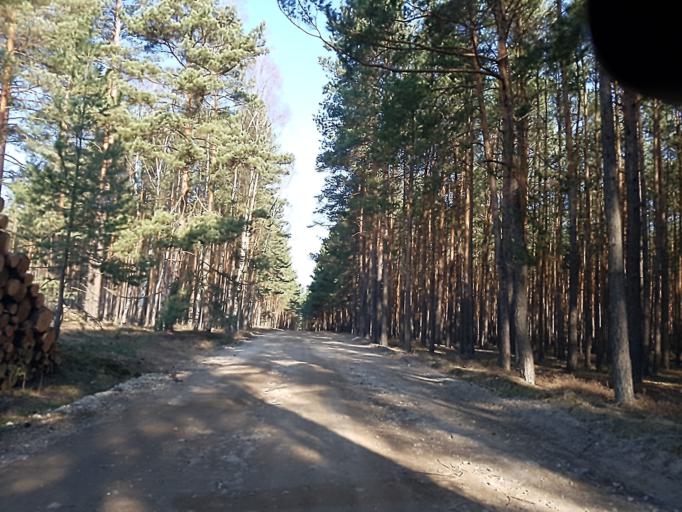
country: DE
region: Brandenburg
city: Tschernitz
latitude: 51.6579
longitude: 14.5683
